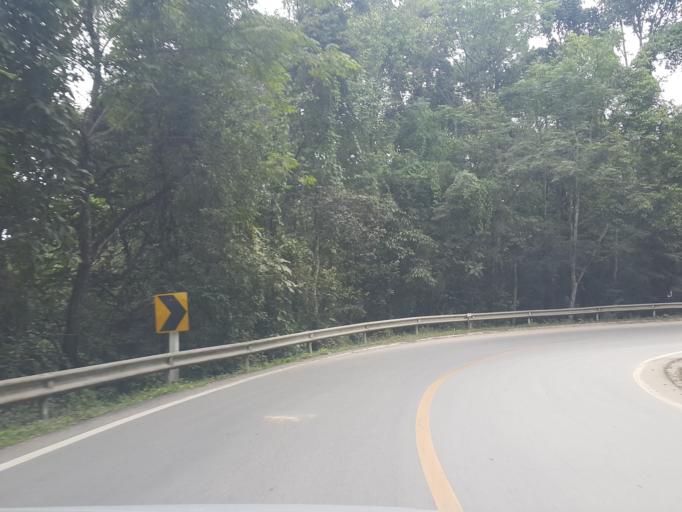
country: TH
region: Mae Hong Son
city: Mae Hi
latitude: 19.2366
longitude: 98.6596
